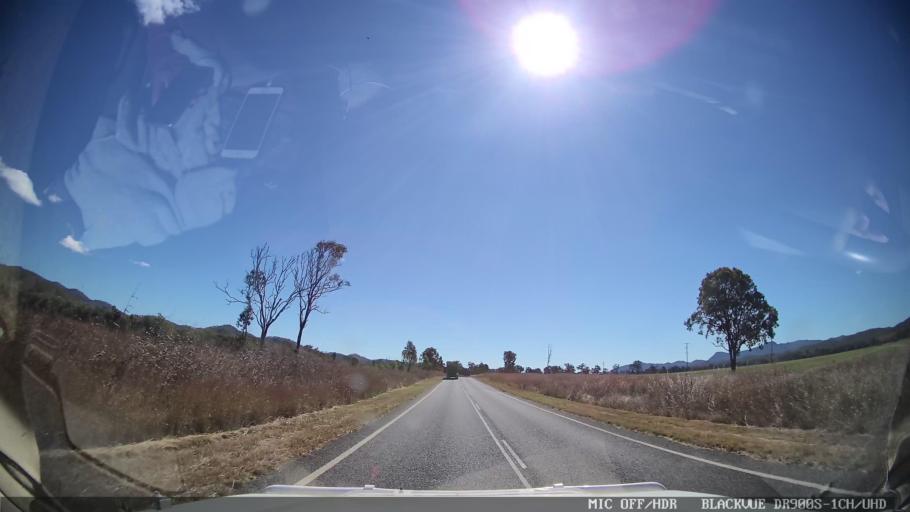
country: AU
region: Queensland
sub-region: Gladstone
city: Toolooa
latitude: -24.2803
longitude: 151.2783
